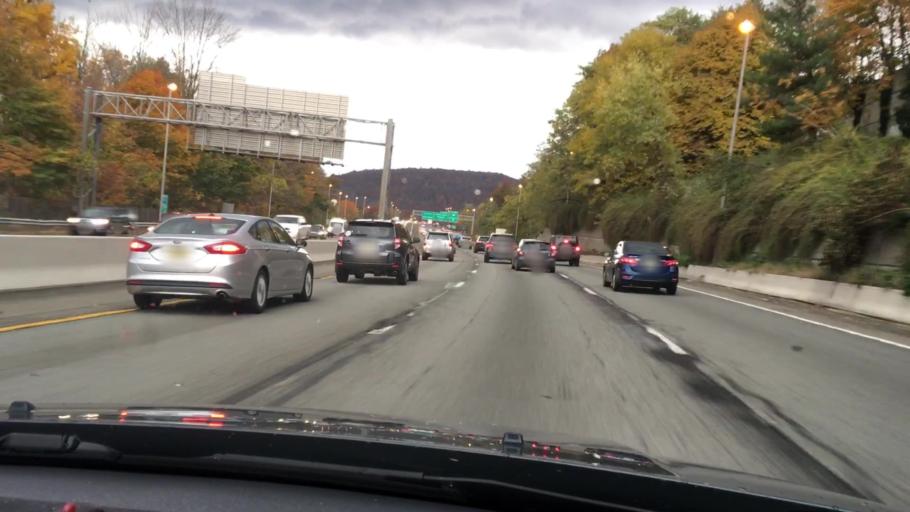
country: US
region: New Jersey
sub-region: Bergen County
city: Franklin Lakes
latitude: 41.0269
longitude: -74.2307
